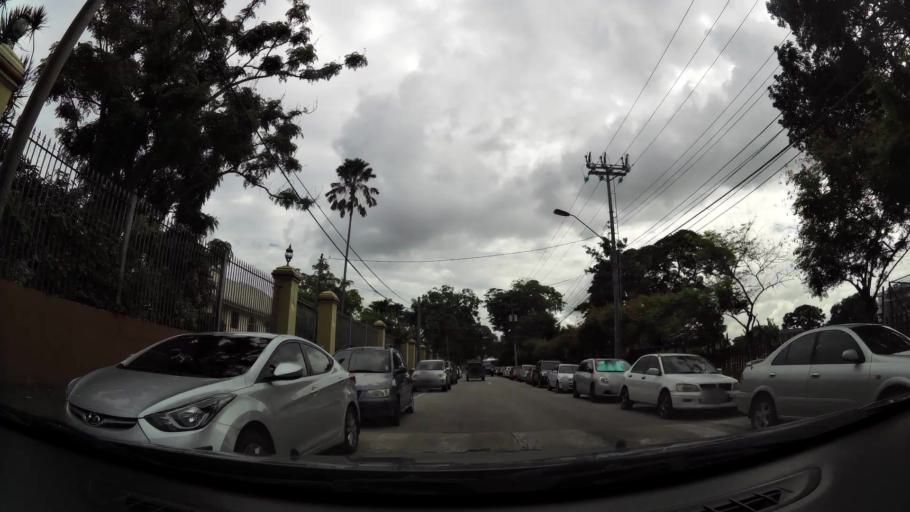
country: TT
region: City of Port of Spain
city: Port-of-Spain
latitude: 10.6696
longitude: -61.5209
